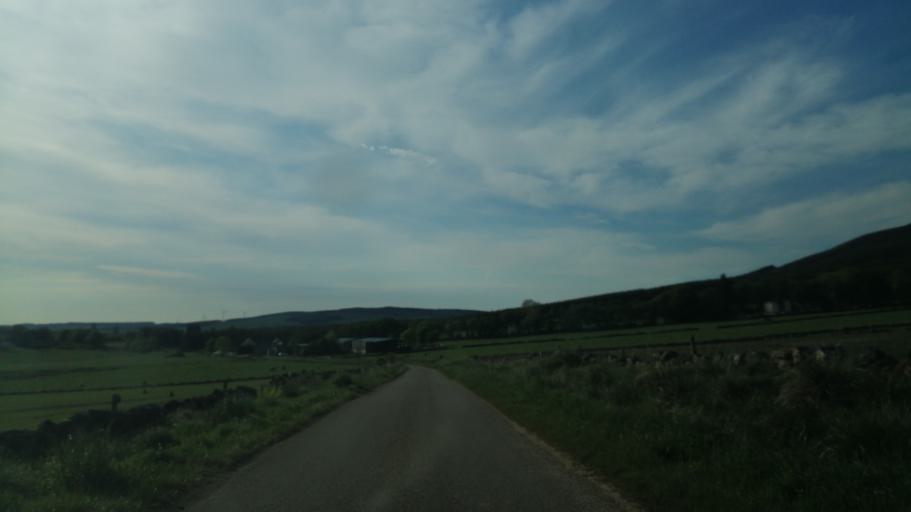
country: GB
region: Scotland
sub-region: Moray
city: Cullen
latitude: 57.5729
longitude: -2.7825
